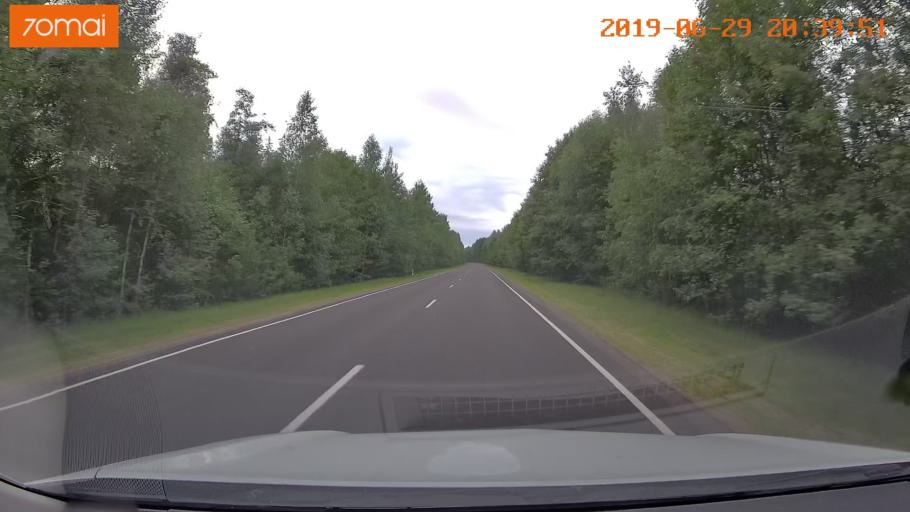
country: BY
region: Brest
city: Hantsavichy
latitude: 52.5675
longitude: 26.3586
